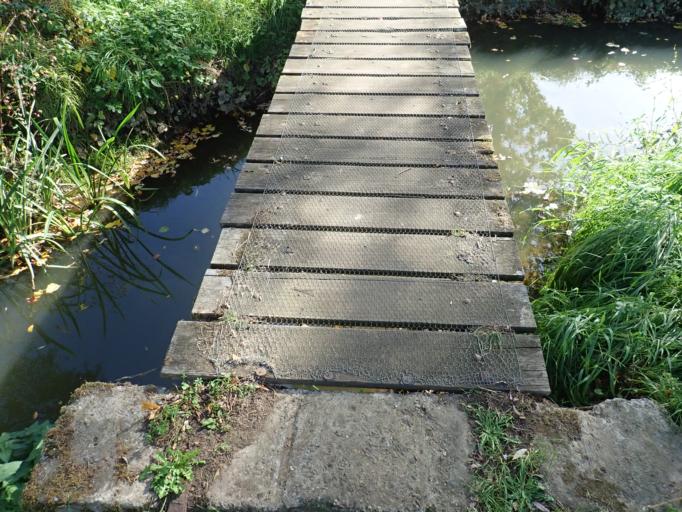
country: BE
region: Flanders
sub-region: Provincie Vlaams-Brabant
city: Holsbeek
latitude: 50.9312
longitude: 4.7585
